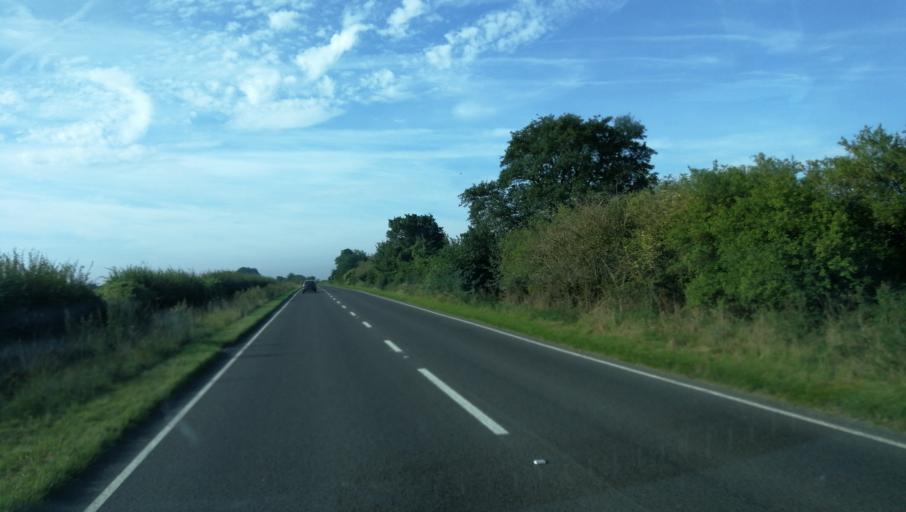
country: GB
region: England
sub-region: Oxfordshire
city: Woodstock
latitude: 51.8898
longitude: -1.3272
